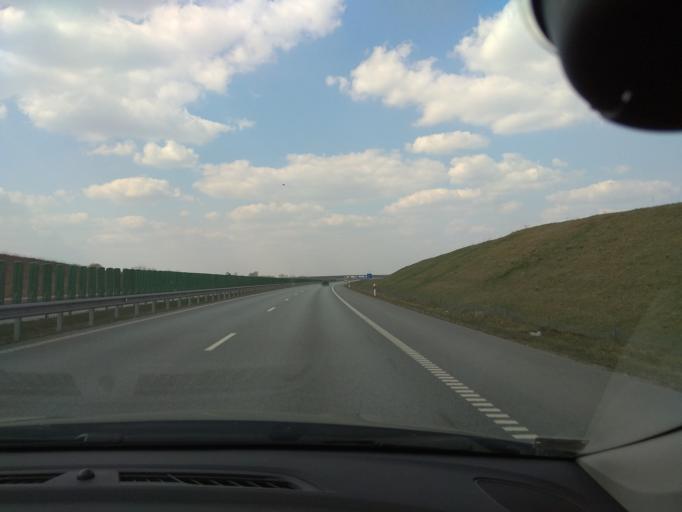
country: LT
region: Siauliu apskritis
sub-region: Siauliai
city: Siauliai
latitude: 55.9099
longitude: 23.4114
